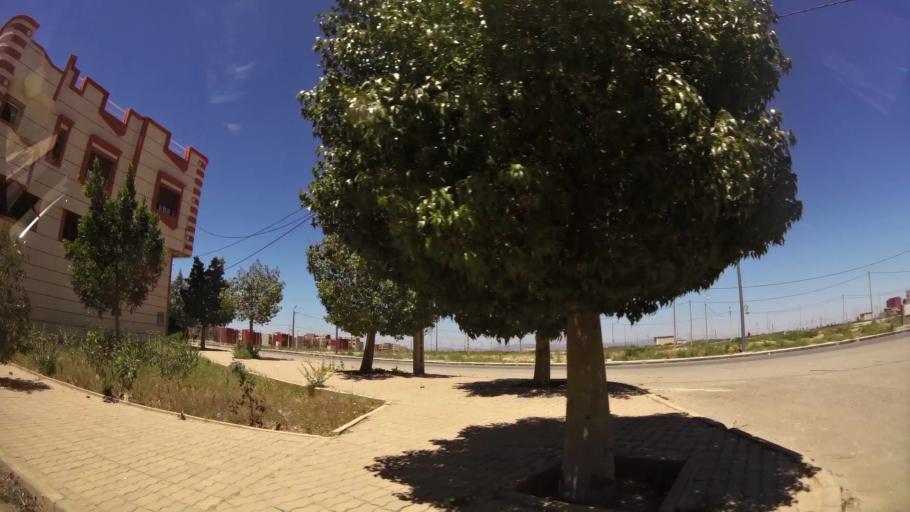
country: MA
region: Oriental
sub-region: Oujda-Angad
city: Oujda
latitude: 34.6789
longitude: -1.8617
